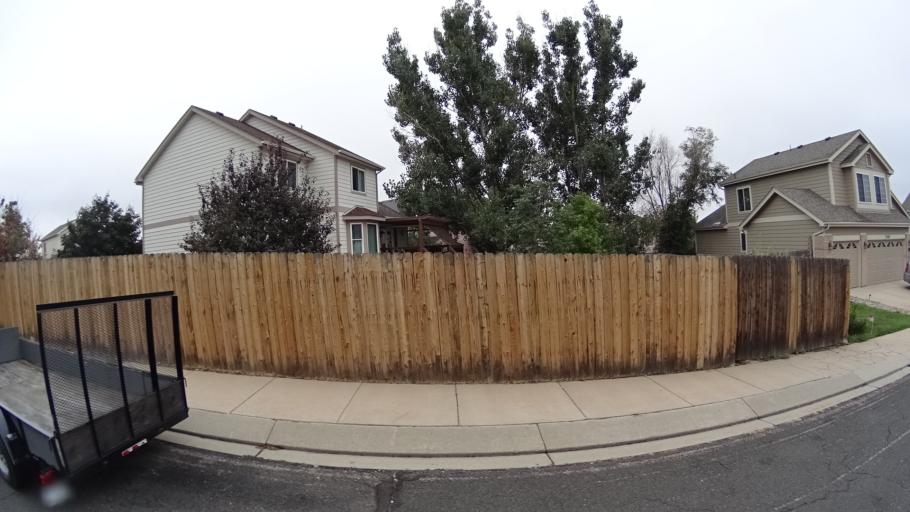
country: US
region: Colorado
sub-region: El Paso County
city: Cimarron Hills
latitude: 38.9347
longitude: -104.7515
